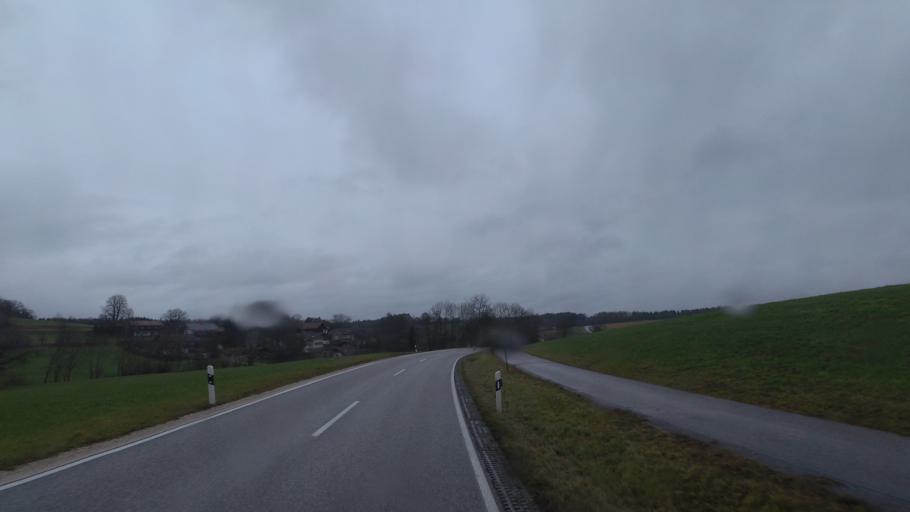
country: DE
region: Bavaria
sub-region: Upper Bavaria
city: Kirchanschoring
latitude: 47.9458
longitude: 12.8126
